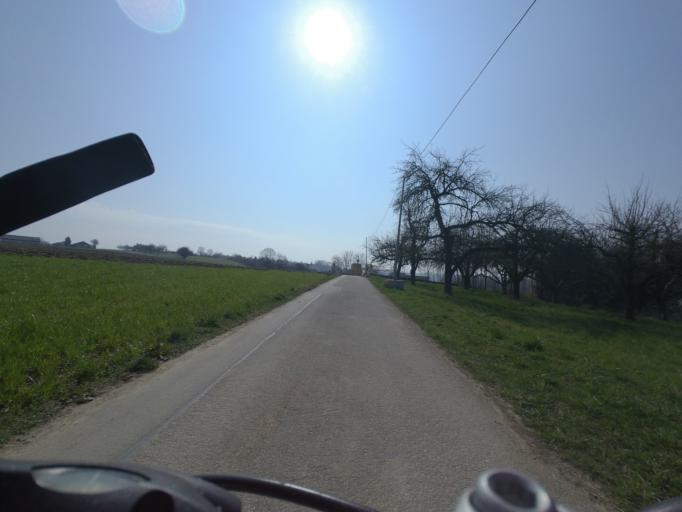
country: DE
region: Baden-Wuerttemberg
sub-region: Regierungsbezirk Stuttgart
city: Oberboihingen
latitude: 48.6595
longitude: 9.3663
